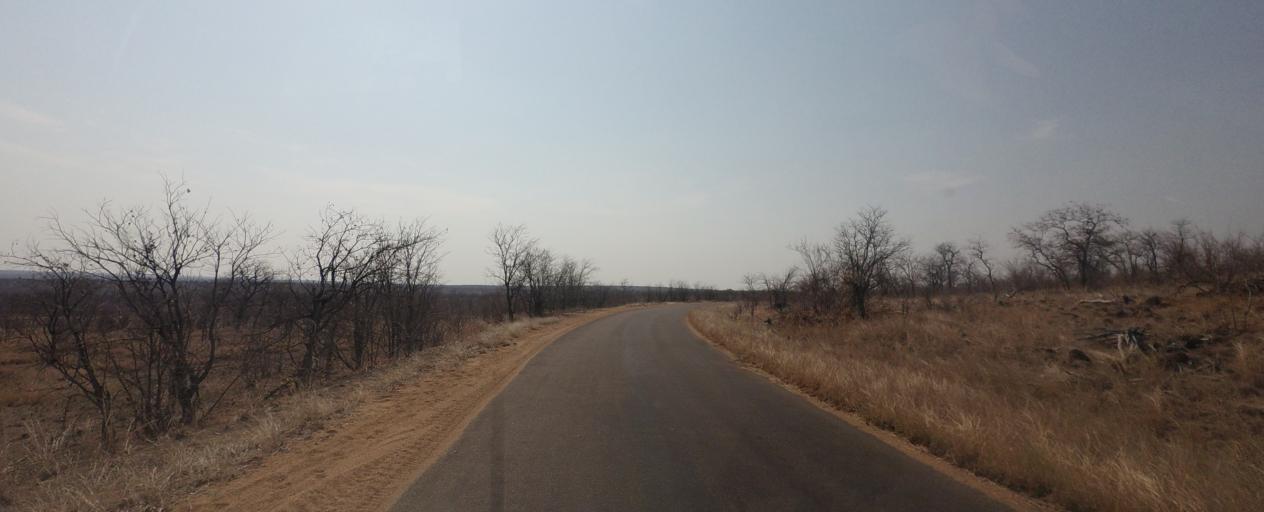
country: ZA
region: Limpopo
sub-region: Mopani District Municipality
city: Phalaborwa
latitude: -23.9707
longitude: 31.6294
